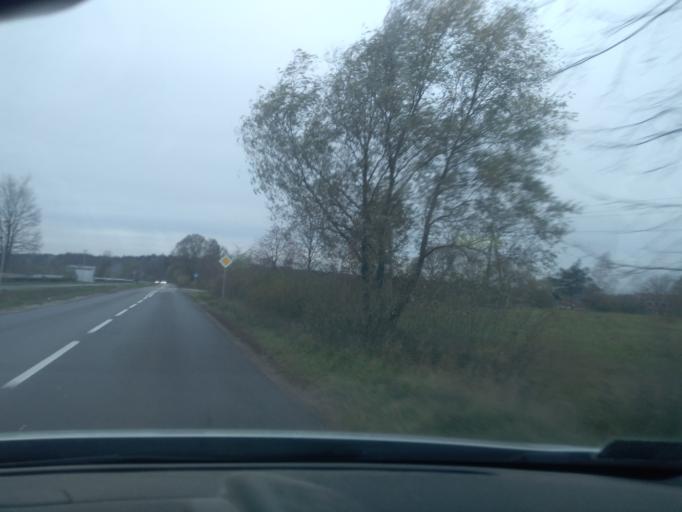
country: PL
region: Greater Poland Voivodeship
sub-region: Powiat poznanski
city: Murowana Goslina
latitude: 52.5592
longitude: 16.9792
